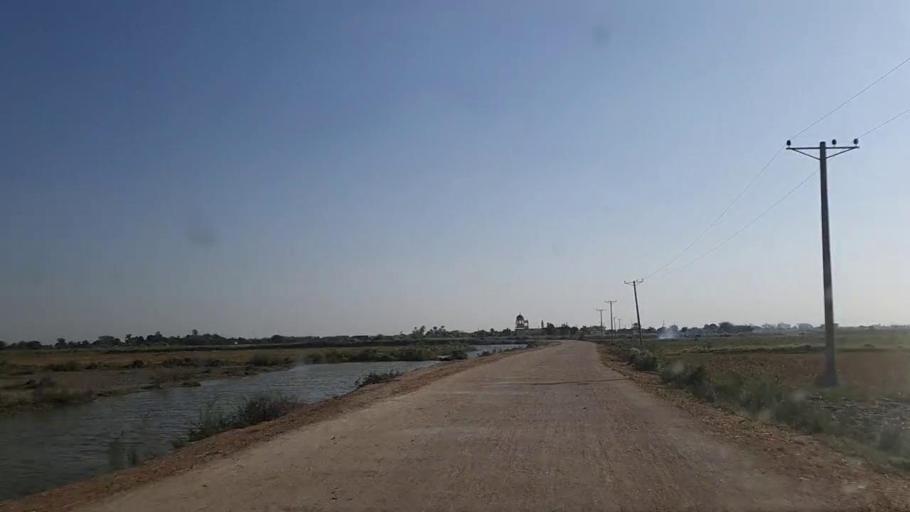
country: PK
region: Sindh
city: Daro Mehar
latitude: 24.6292
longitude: 68.0792
